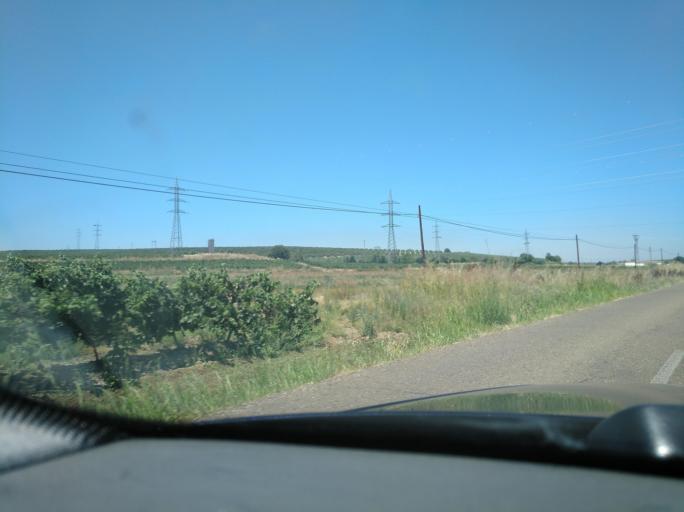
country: ES
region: Extremadura
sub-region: Provincia de Badajoz
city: Olivenza
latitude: 38.7368
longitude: -7.0626
